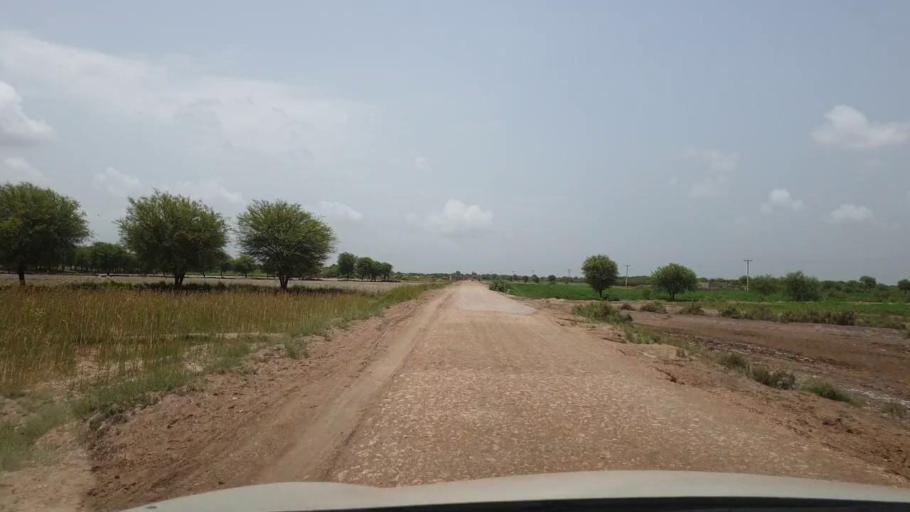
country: PK
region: Sindh
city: Chambar
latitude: 25.2019
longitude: 68.7619
